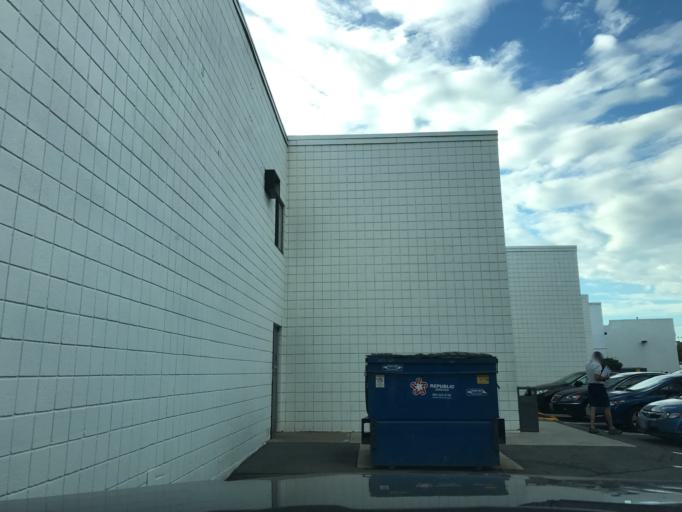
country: US
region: Massachusetts
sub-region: Middlesex County
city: Watertown
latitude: 42.3647
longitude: -71.1588
